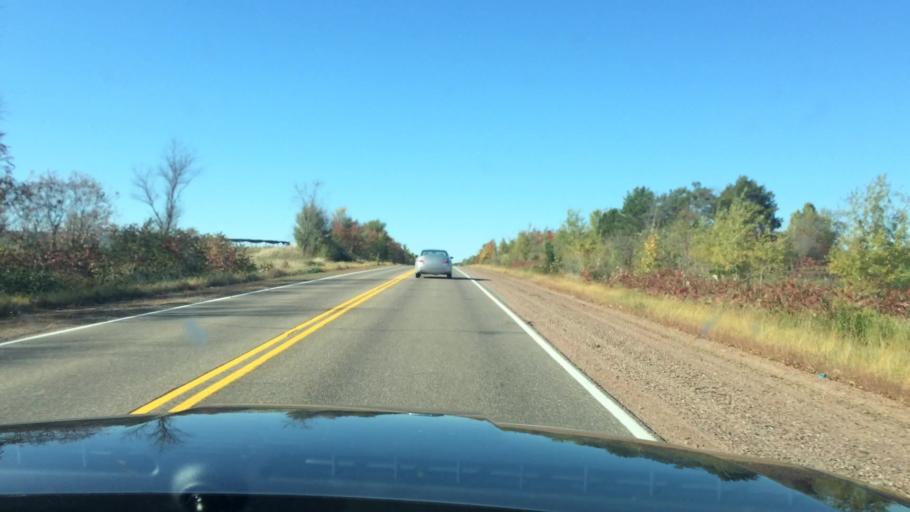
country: US
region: Wisconsin
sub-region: Marathon County
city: Wausau
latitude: 45.0058
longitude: -89.6719
